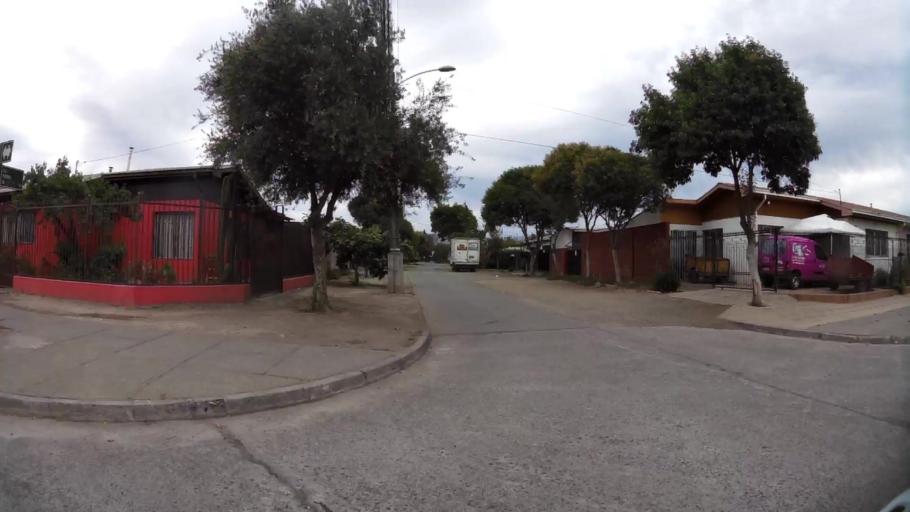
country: CL
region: O'Higgins
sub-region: Provincia de Cachapoal
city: Rancagua
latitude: -34.1603
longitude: -70.7479
